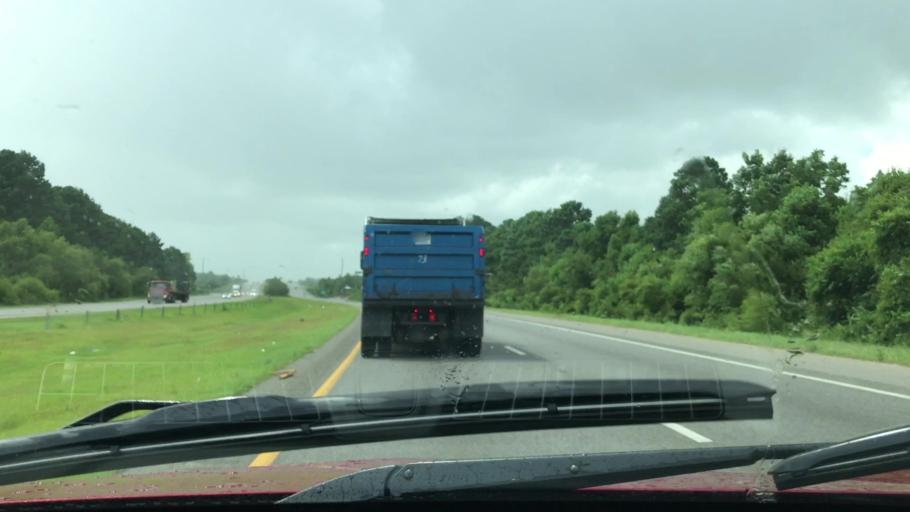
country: US
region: South Carolina
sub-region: Charleston County
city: Mount Pleasant
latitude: 32.8357
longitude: -79.8551
